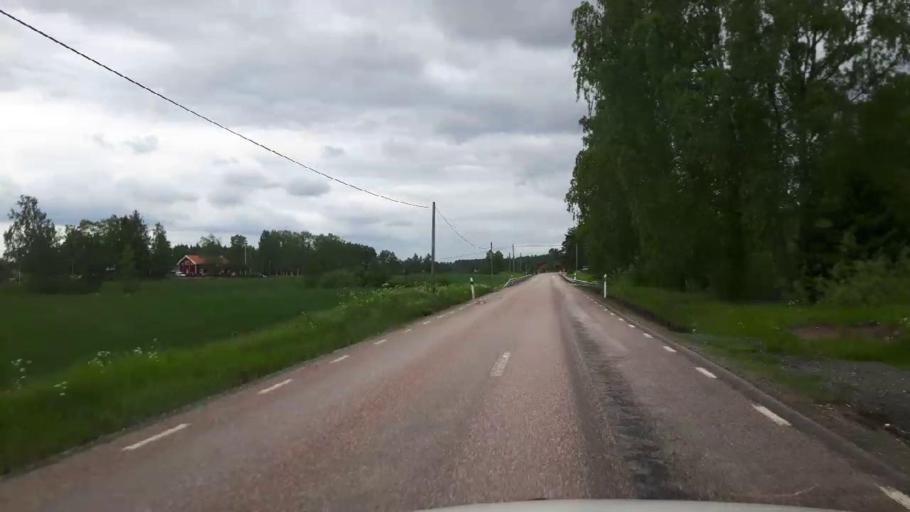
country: SE
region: Vaestmanland
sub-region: Kopings Kommun
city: Kolsva
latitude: 59.7330
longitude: 15.8034
